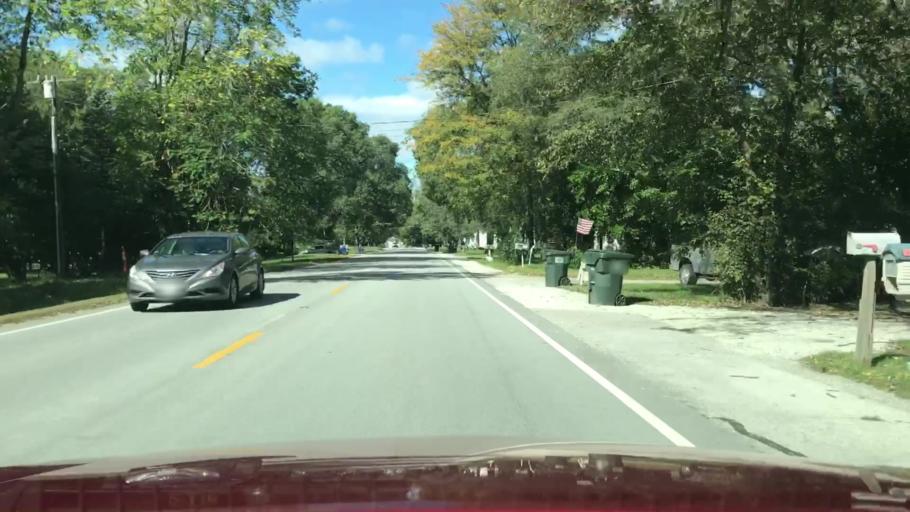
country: US
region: Illinois
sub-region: Cook County
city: Lynwood
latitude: 41.5197
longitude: -87.5489
